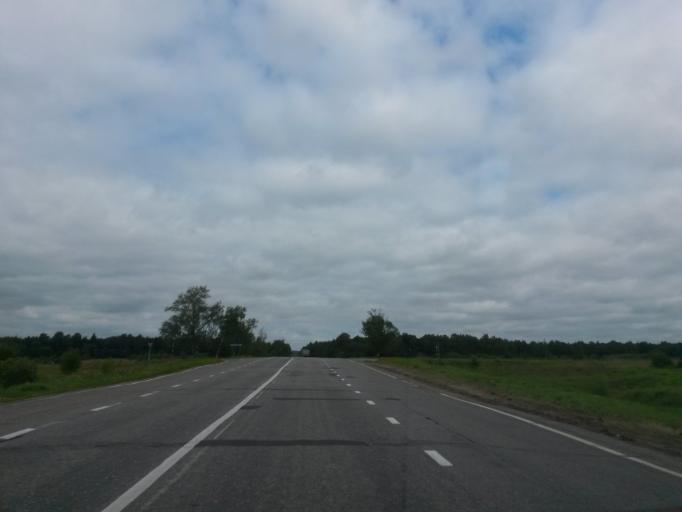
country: RU
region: Jaroslavl
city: Gavrilov-Yam
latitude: 57.4464
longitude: 39.9150
